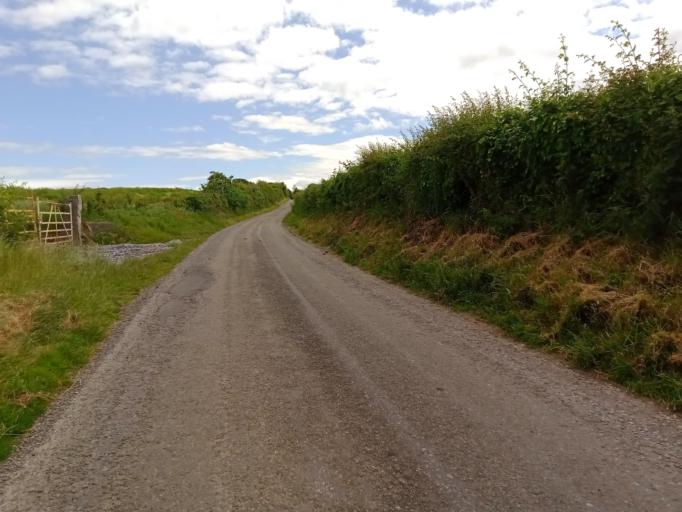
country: IE
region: Leinster
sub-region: Kilkenny
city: Kilkenny
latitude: 52.6817
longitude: -7.2480
